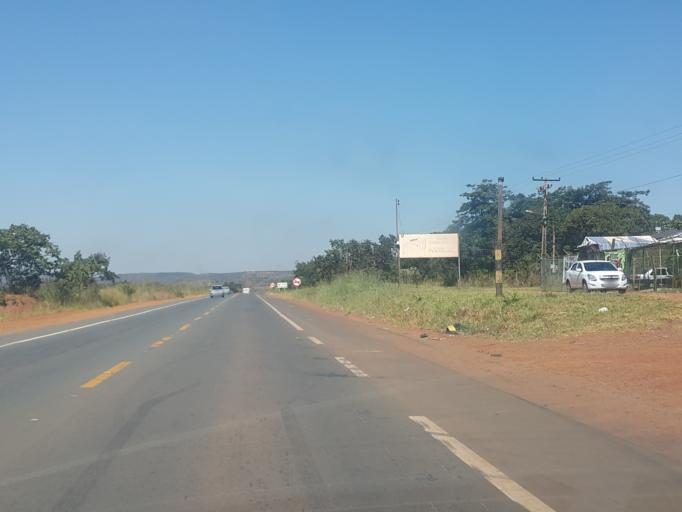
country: BR
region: Goias
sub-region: Luziania
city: Luziania
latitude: -16.0114
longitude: -48.1451
